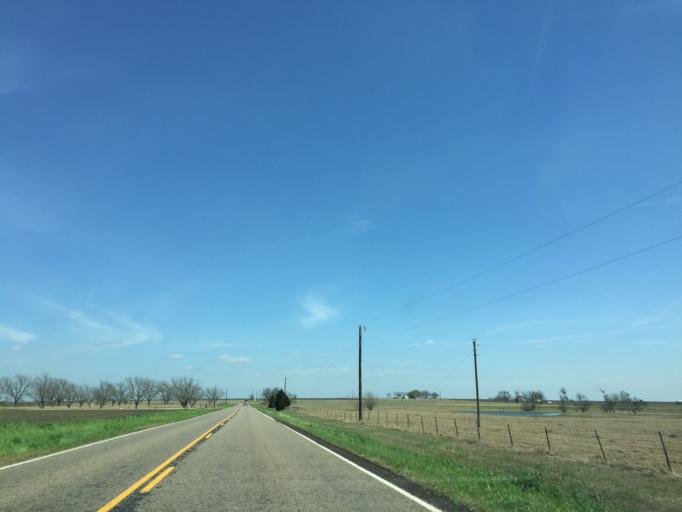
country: US
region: Texas
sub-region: Williamson County
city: Taylor
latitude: 30.5697
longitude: -97.3375
